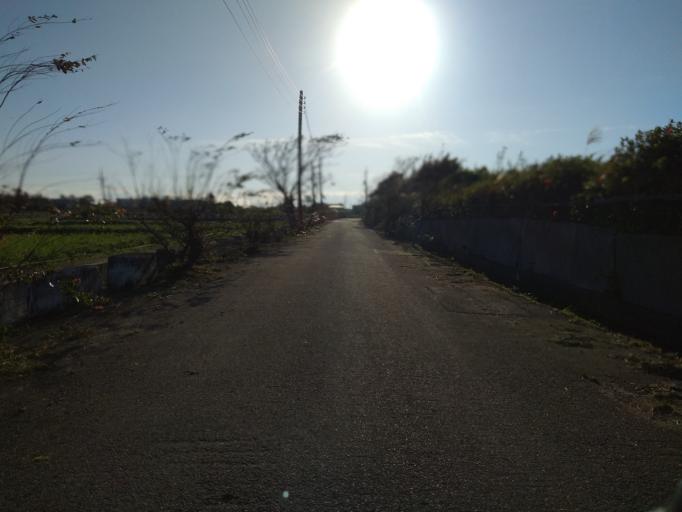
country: TW
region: Taiwan
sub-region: Hsinchu
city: Zhubei
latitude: 24.9859
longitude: 121.0538
